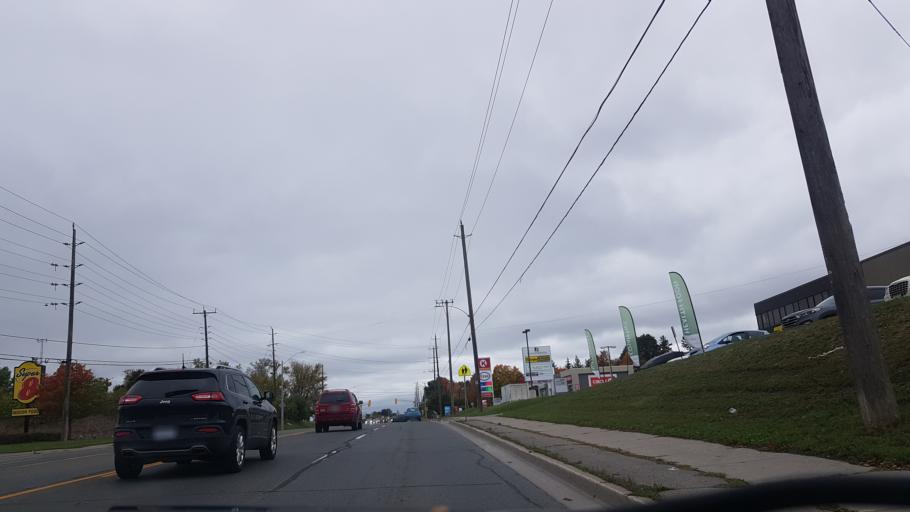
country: CA
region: Ontario
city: Peterborough
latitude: 44.2801
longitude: -78.3535
